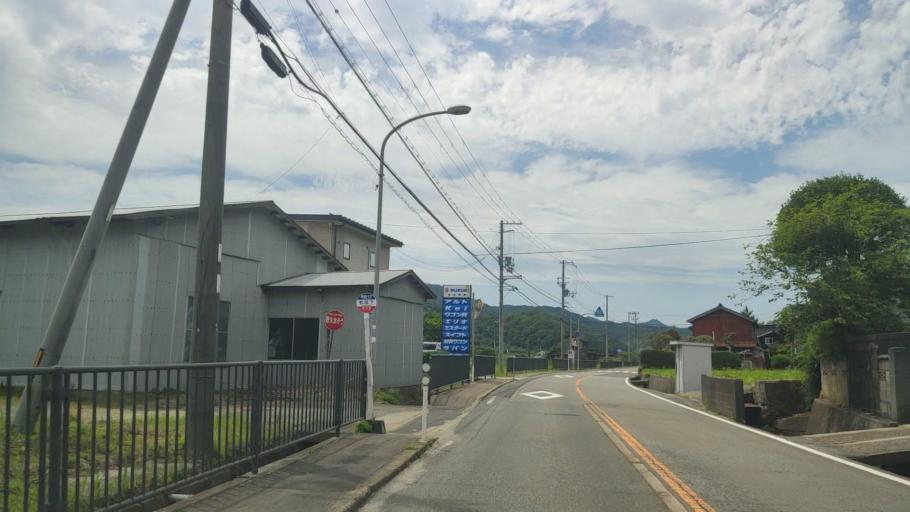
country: JP
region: Hyogo
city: Toyooka
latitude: 35.6457
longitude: 134.7580
